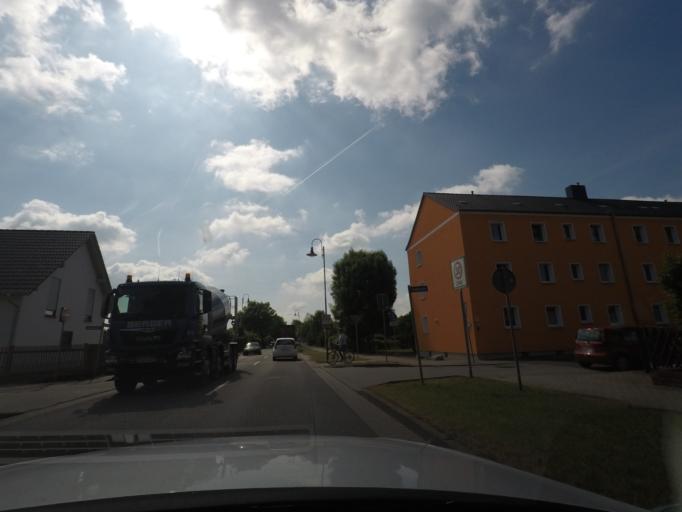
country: DE
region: Saxony
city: Markranstadt
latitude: 51.2974
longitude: 12.2251
